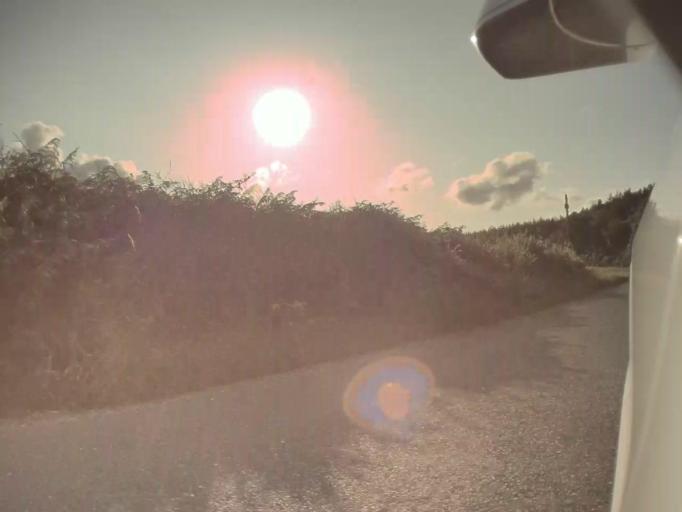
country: IE
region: Leinster
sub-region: Wicklow
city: Enniskerry
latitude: 53.1880
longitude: -6.2223
